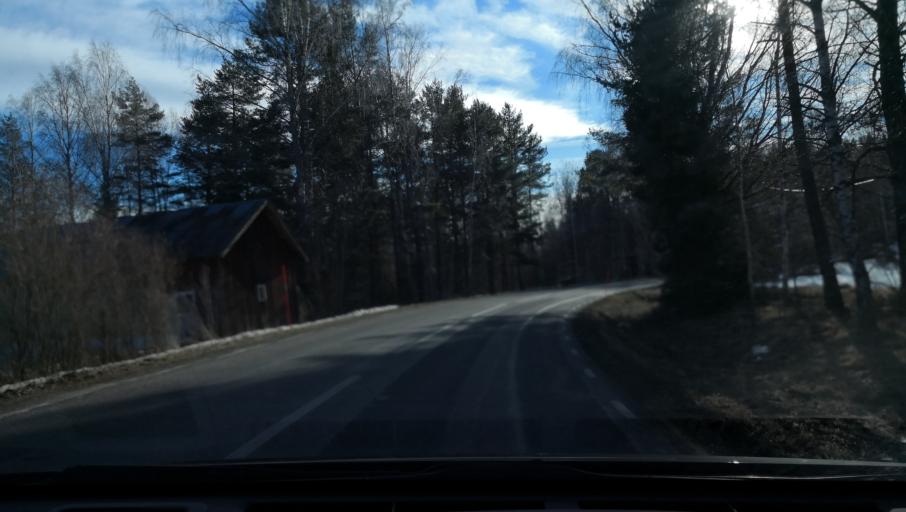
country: SE
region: Uppsala
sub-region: Osthammars Kommun
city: Osterbybruk
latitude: 60.2919
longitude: 18.0469
